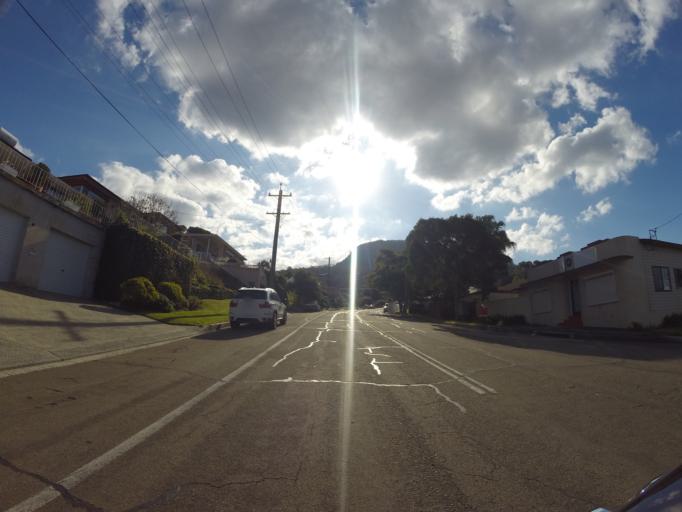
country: AU
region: New South Wales
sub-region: Wollongong
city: Mount Keira
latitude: -34.4142
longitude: 150.8588
